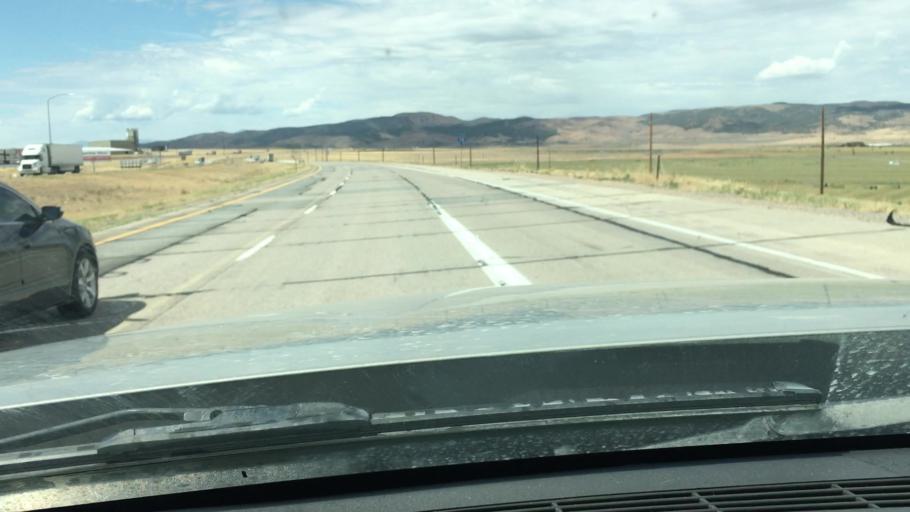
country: US
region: Utah
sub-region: Juab County
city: Nephi
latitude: 39.6817
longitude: -111.8409
